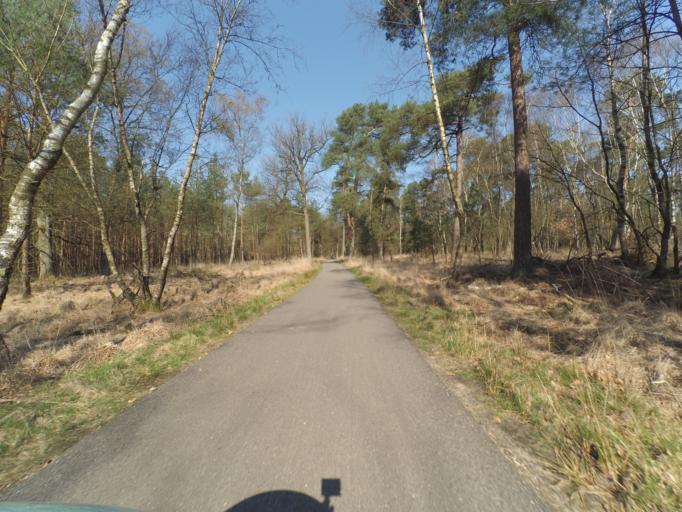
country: NL
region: Gelderland
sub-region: Gemeente Ede
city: Otterlo
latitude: 52.0992
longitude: 5.8600
